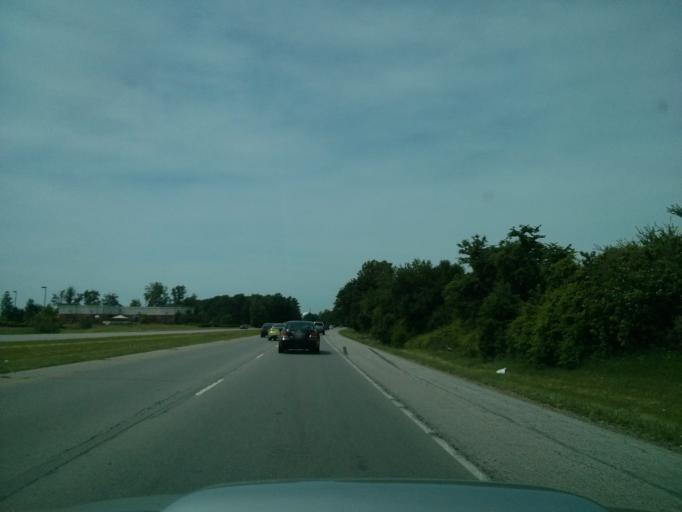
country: US
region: Indiana
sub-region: Hamilton County
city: Noblesville
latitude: 40.0196
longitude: -85.9989
